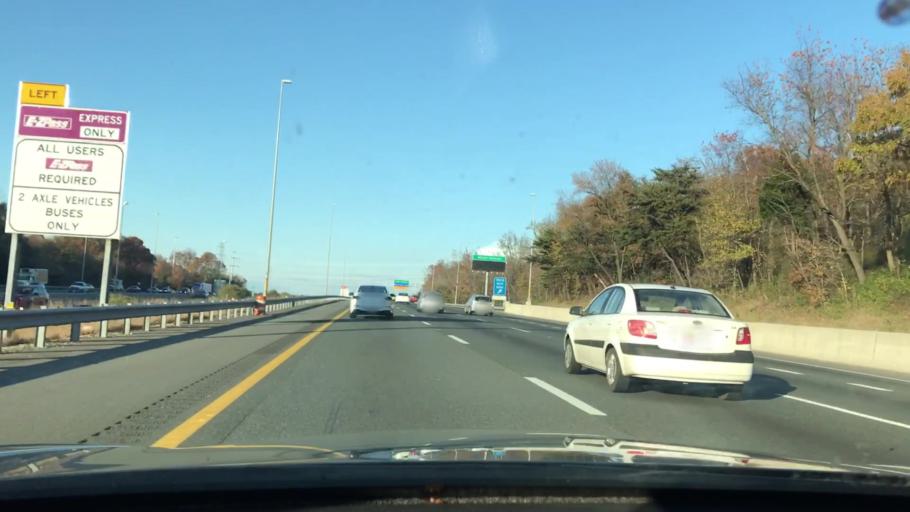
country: US
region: Virginia
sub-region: Prince William County
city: Dumfries
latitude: 38.5893
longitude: -77.3178
